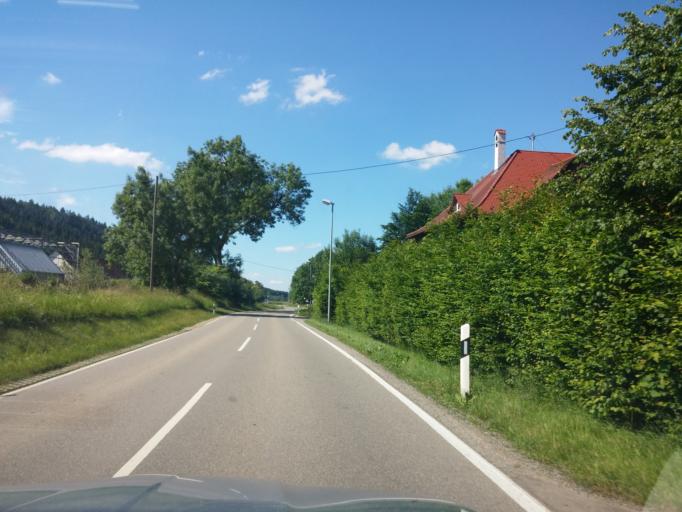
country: DE
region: Baden-Wuerttemberg
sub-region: Tuebingen Region
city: Aitrach
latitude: 47.9465
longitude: 10.0809
